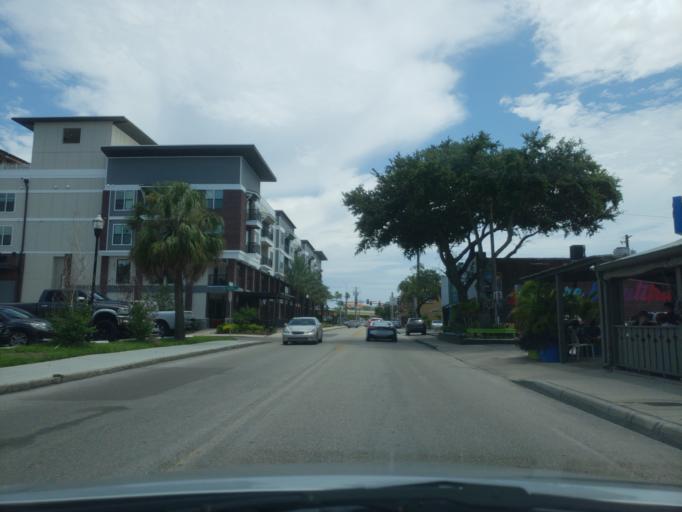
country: US
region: Florida
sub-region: Hillsborough County
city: Tampa
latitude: 27.9351
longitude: -82.4831
